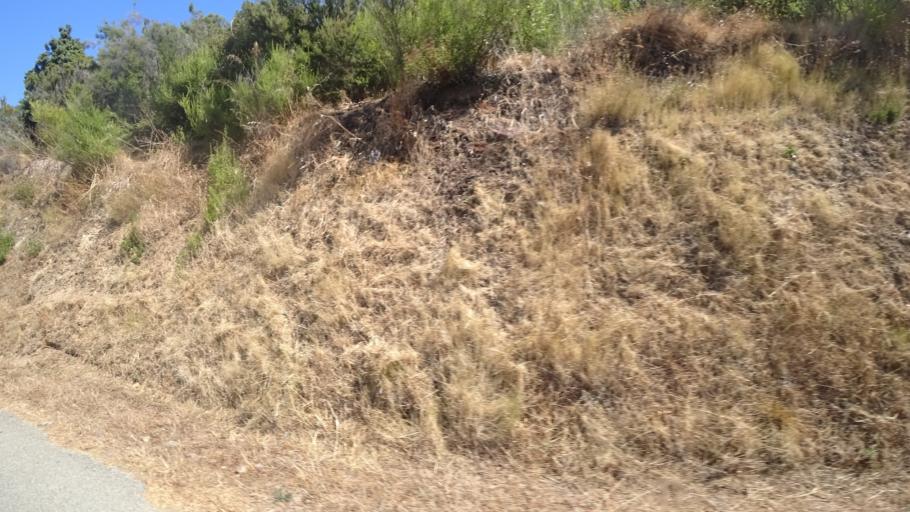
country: FR
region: Corsica
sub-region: Departement de la Corse-du-Sud
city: Alata
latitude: 41.9699
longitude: 8.6954
